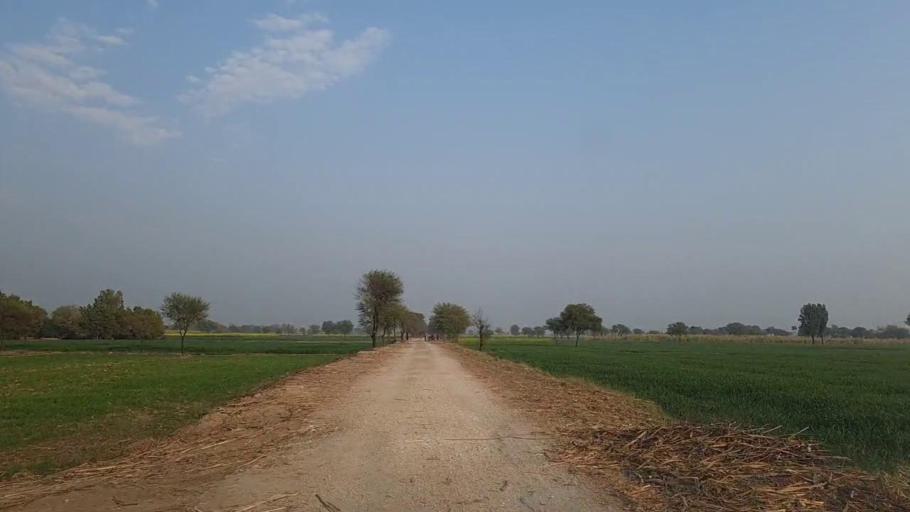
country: PK
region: Sindh
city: Jam Sahib
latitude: 26.3256
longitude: 68.5606
